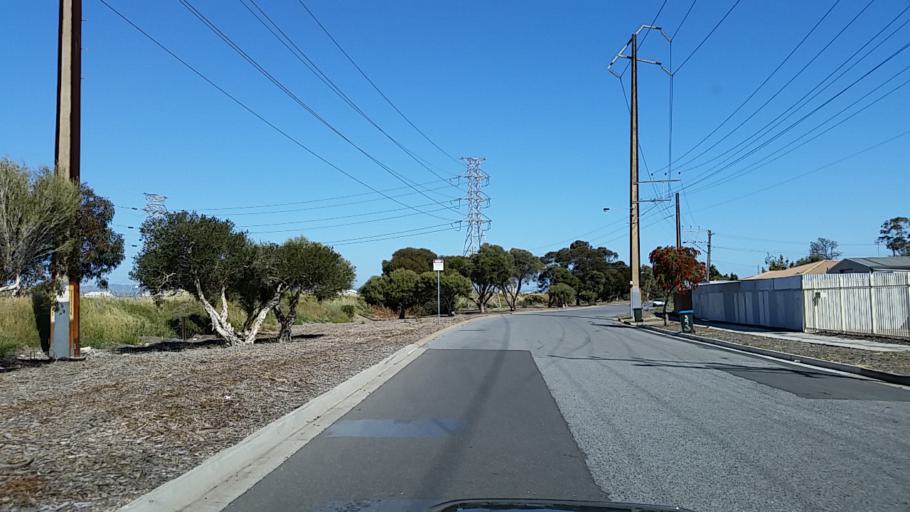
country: AU
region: South Australia
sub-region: Port Adelaide Enfield
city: Birkenhead
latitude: -34.8048
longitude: 138.5060
